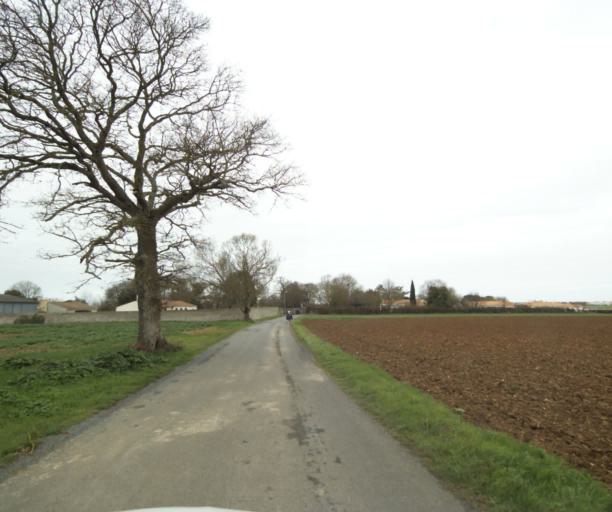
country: FR
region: Poitou-Charentes
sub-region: Departement de la Charente-Maritime
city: Nieul-sur-Mer
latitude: 46.1931
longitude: -1.1698
